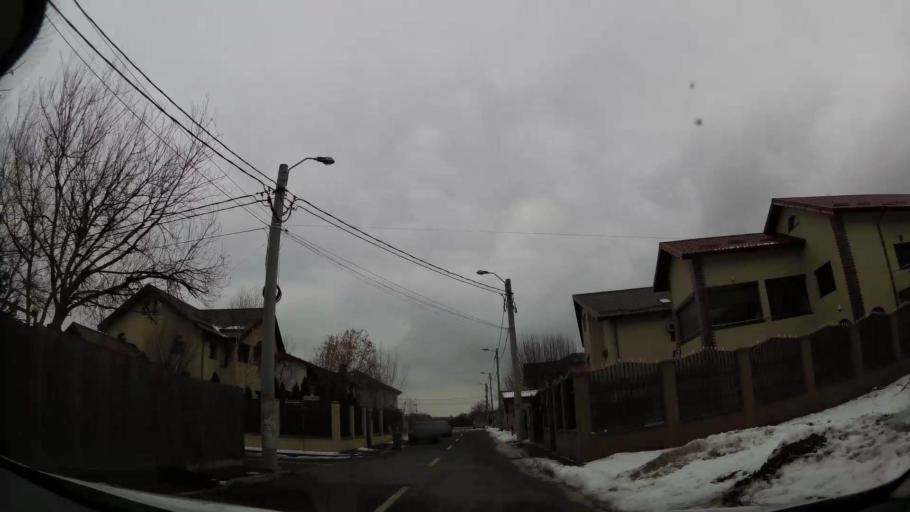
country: RO
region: Ilfov
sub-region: Comuna Otopeni
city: Otopeni
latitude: 44.5533
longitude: 26.0919
